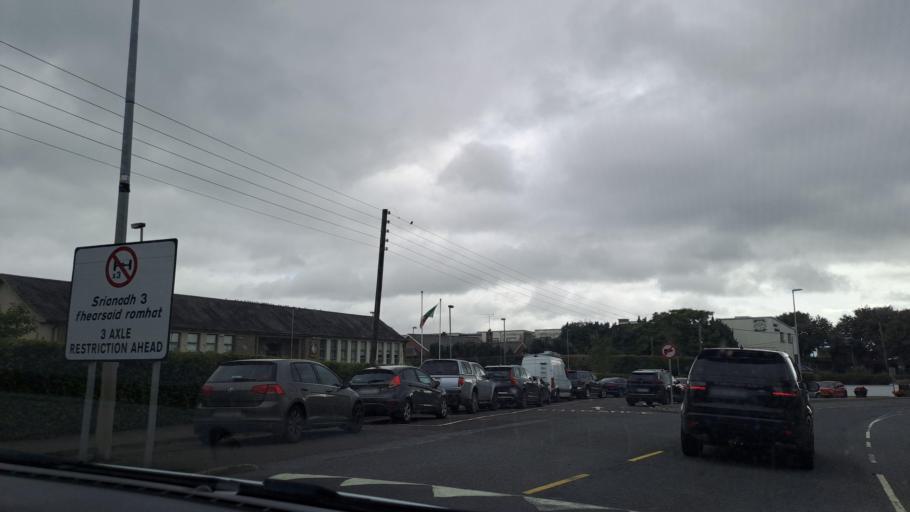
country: IE
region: Ulster
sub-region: County Monaghan
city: Carrickmacross
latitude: 53.9837
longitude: -6.7172
